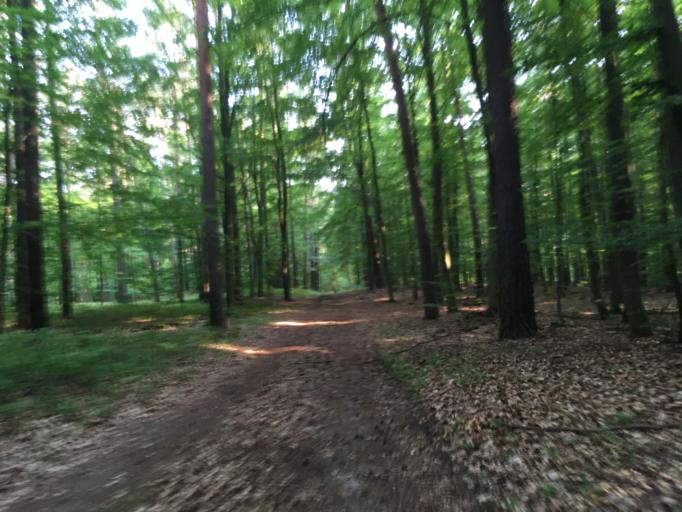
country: DE
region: Brandenburg
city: Wandlitz
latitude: 52.7281
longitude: 13.5286
